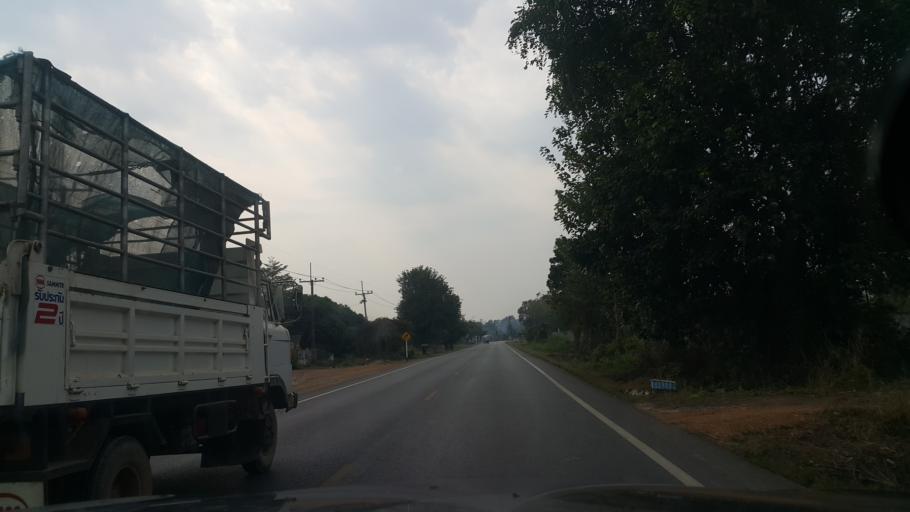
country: TH
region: Sukhothai
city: Si Samrong
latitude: 17.1102
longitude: 99.8892
